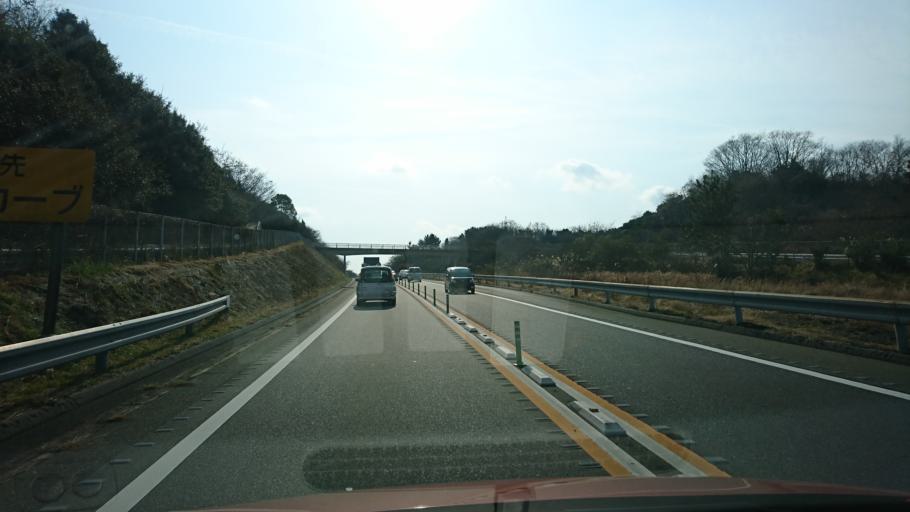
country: JP
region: Hiroshima
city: Onomichi
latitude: 34.3678
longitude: 133.1909
